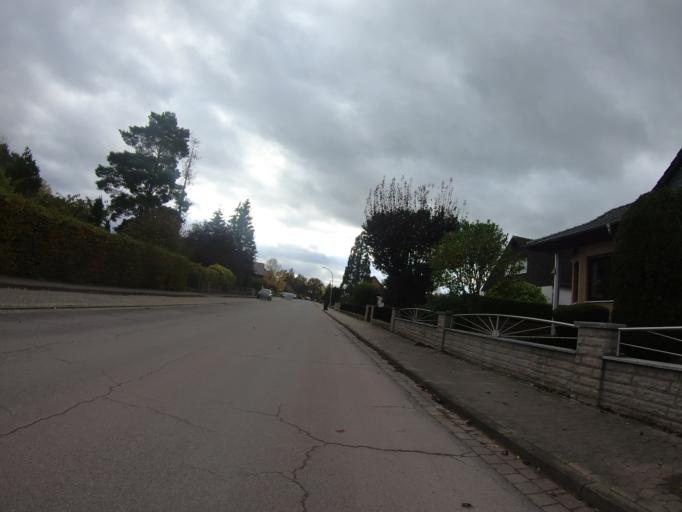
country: DE
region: Lower Saxony
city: Adenbuettel
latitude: 52.3796
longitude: 10.4833
